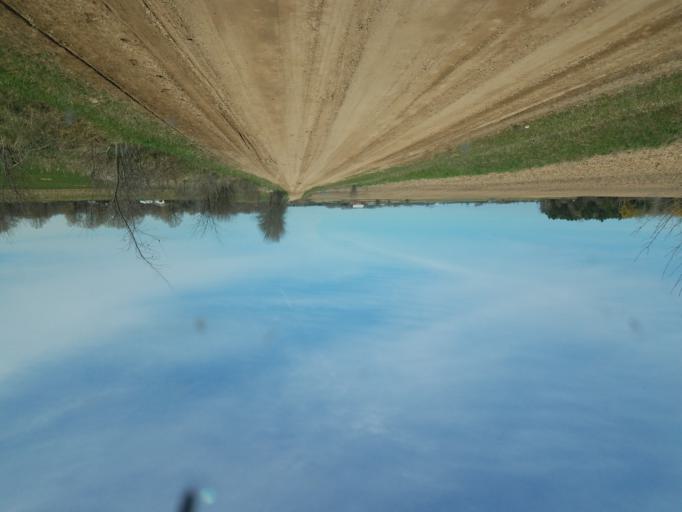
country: US
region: Michigan
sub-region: Gladwin County
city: Gladwin
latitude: 44.0599
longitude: -84.4827
